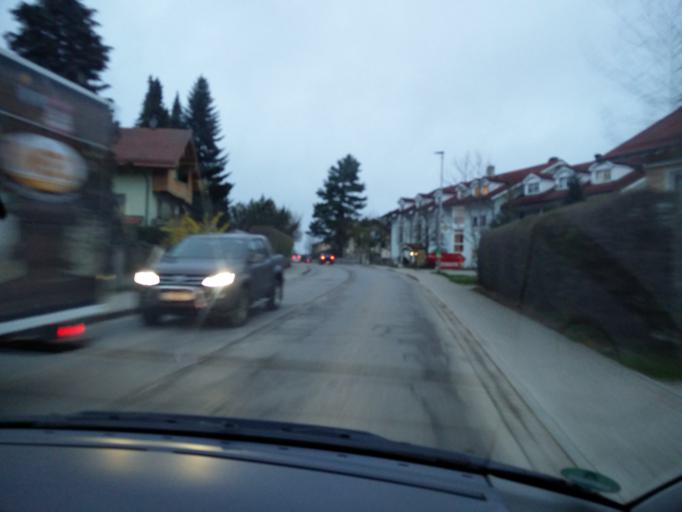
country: DE
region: Bavaria
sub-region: Upper Bavaria
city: Bad Endorf
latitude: 47.9099
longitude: 12.2970
